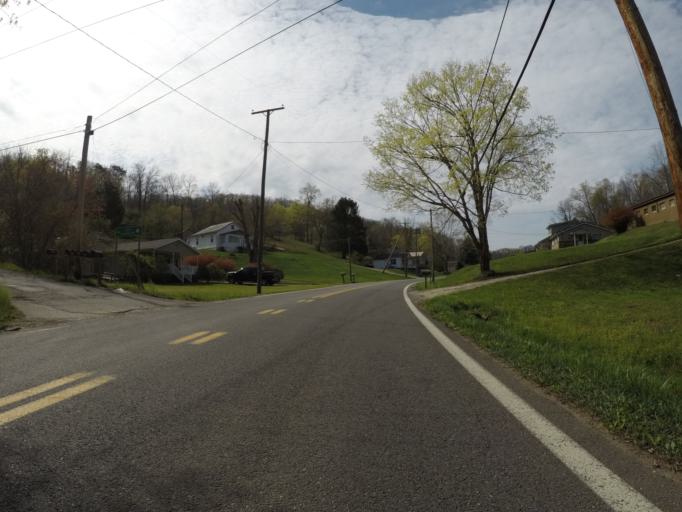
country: US
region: West Virginia
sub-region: Cabell County
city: Pea Ridge
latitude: 38.3716
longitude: -82.3708
